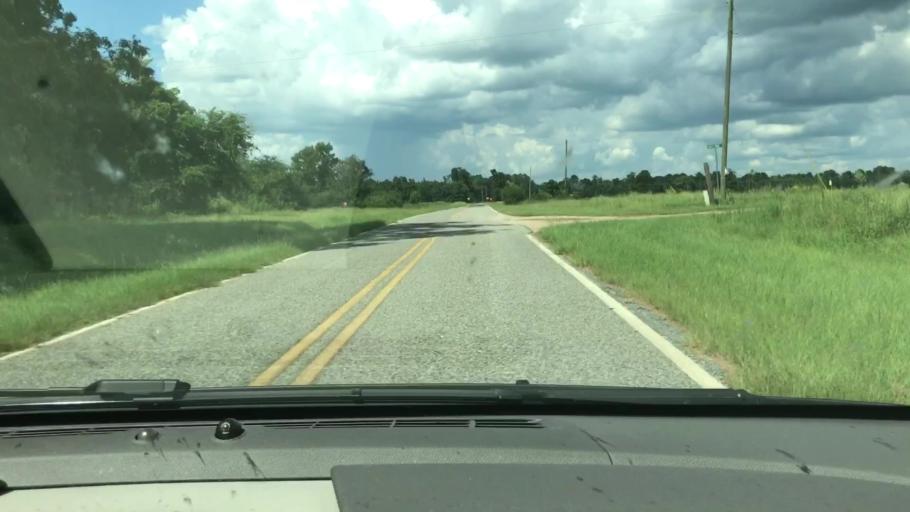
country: US
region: Georgia
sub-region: Quitman County
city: Georgetown
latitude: 31.7545
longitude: -85.0742
